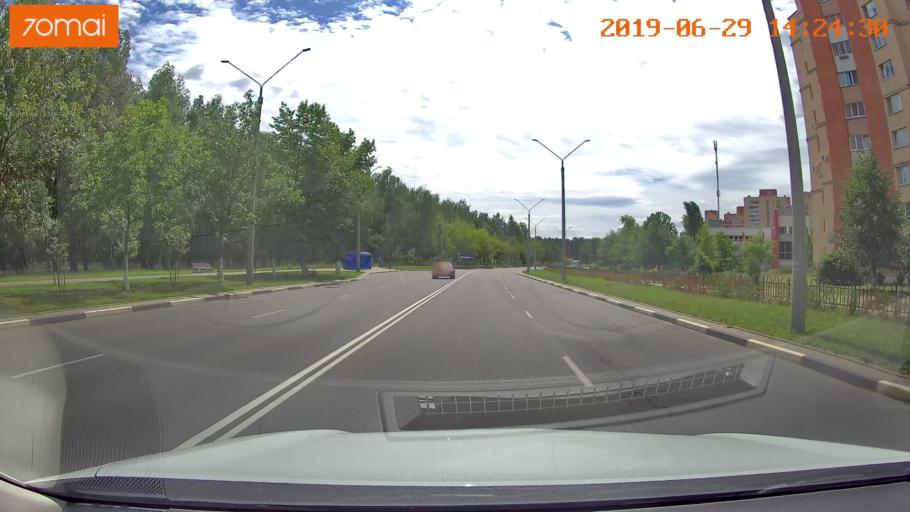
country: BY
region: Minsk
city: Salihorsk
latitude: 52.7807
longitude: 27.5489
